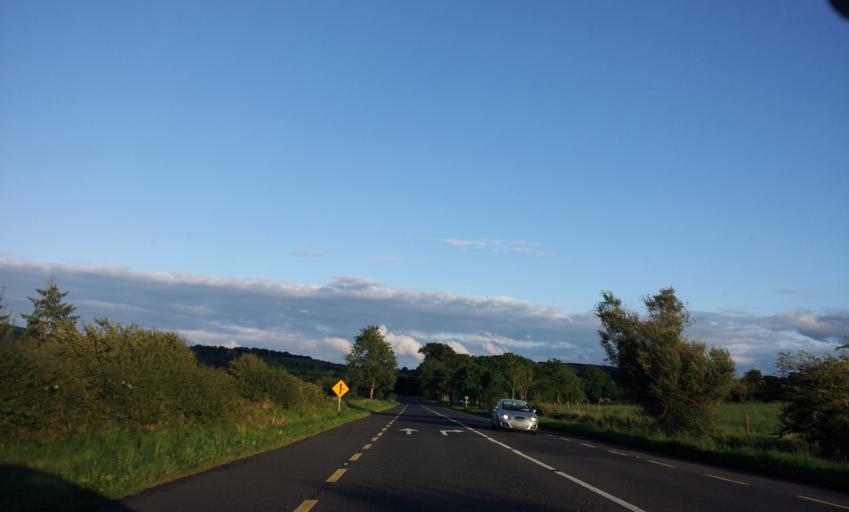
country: IE
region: Munster
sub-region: County Limerick
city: Abbeyfeale
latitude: 52.3850
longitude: -9.2299
